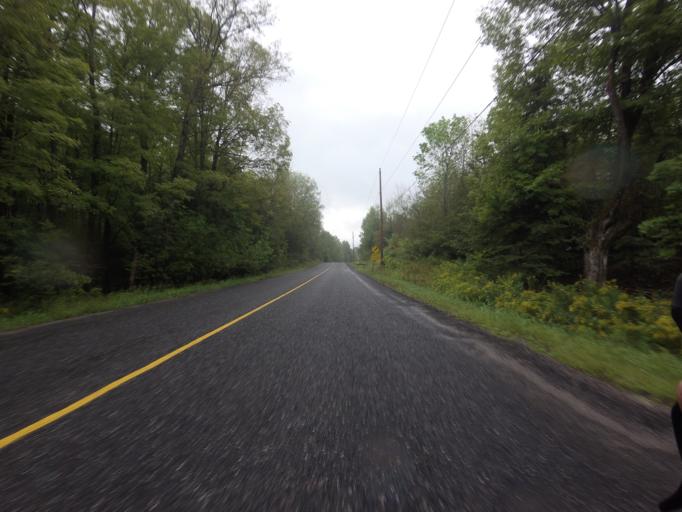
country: CA
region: Ontario
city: Perth
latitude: 45.0624
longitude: -76.5324
